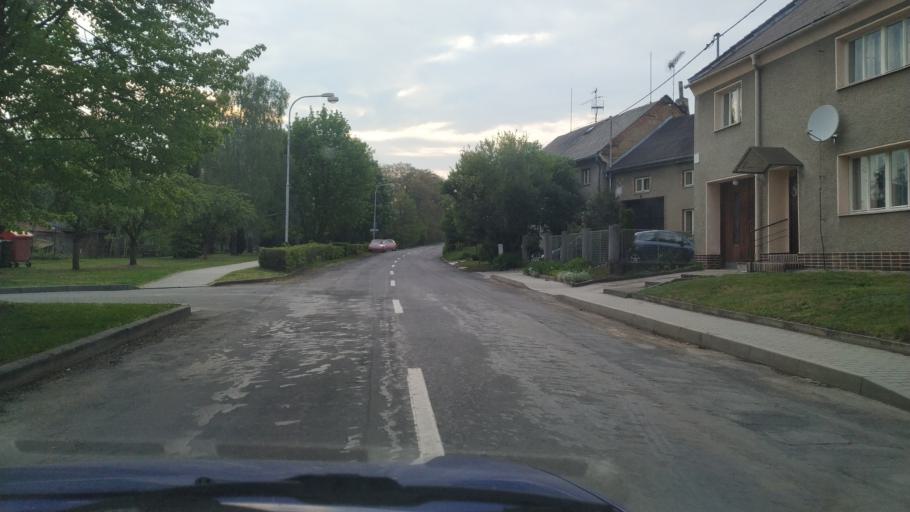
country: CZ
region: Olomoucky
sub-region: Okres Olomouc
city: Slatinice
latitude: 49.5511
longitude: 17.1104
